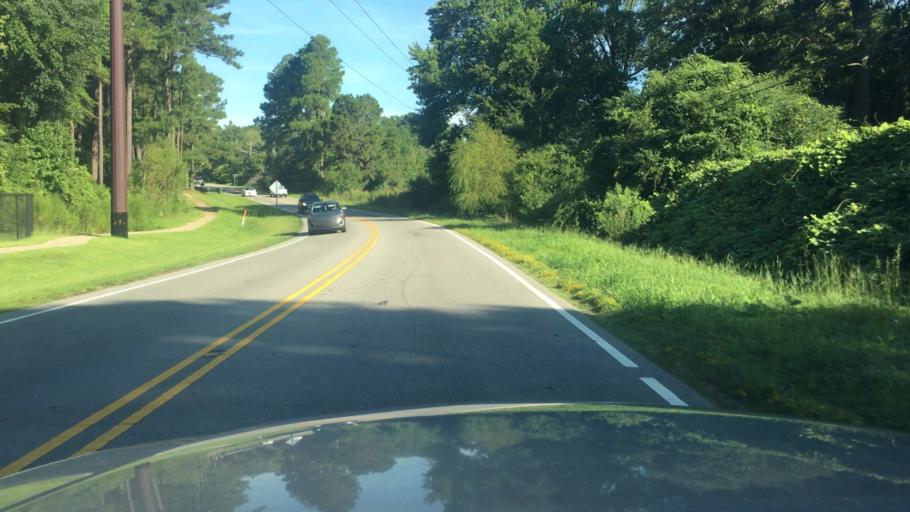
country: US
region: North Carolina
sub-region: Cumberland County
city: Fayetteville
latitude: 35.1254
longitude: -78.8884
